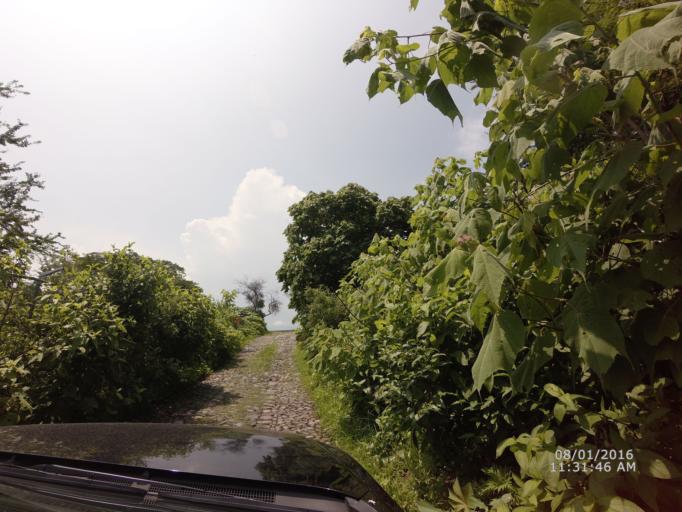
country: MX
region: Nayarit
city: Jala
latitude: 21.1077
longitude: -104.4493
